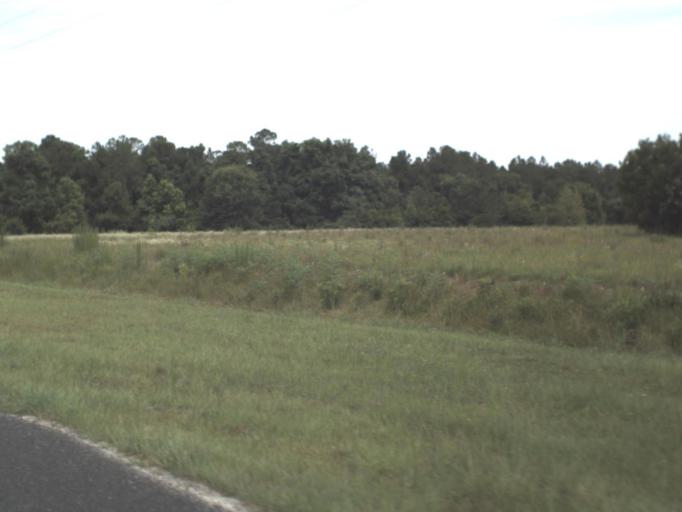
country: US
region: Florida
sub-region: Alachua County
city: Hawthorne
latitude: 29.5985
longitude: -82.1183
